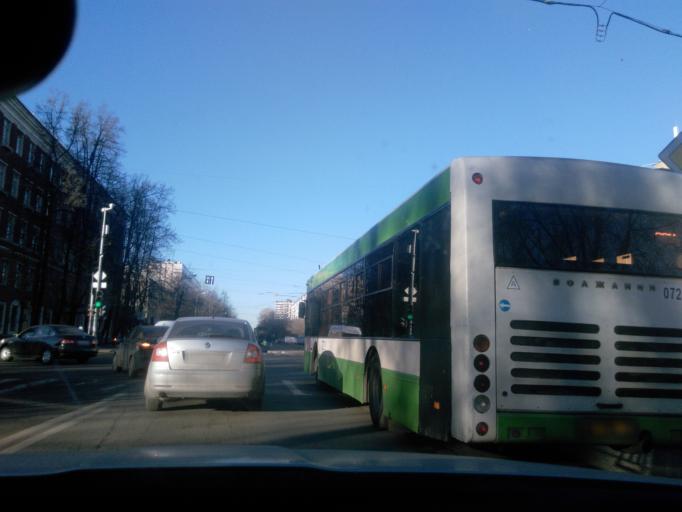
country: RU
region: Moskovskaya
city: Koptevo
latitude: 55.8229
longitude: 37.5185
